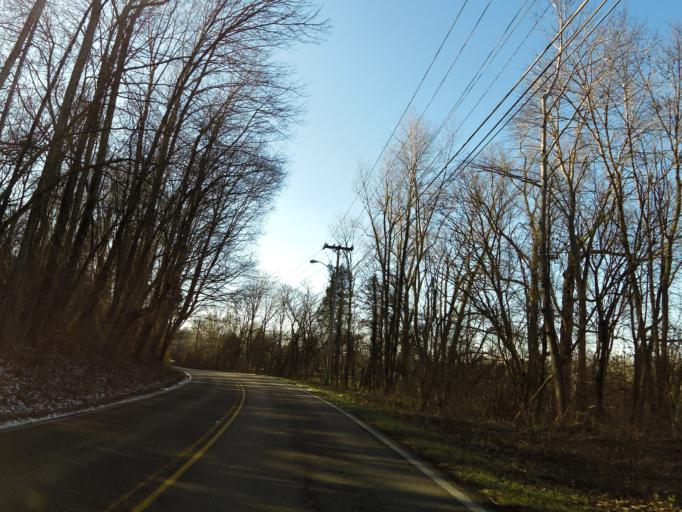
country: US
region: Tennessee
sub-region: Knox County
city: Knoxville
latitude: 35.9158
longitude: -83.9906
